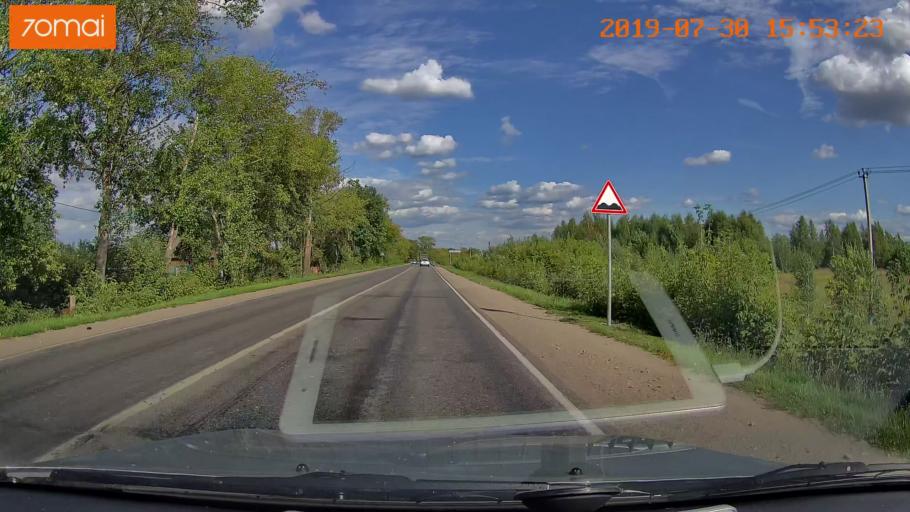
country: RU
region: Moskovskaya
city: Voskresensk
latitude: 55.3202
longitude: 38.6390
